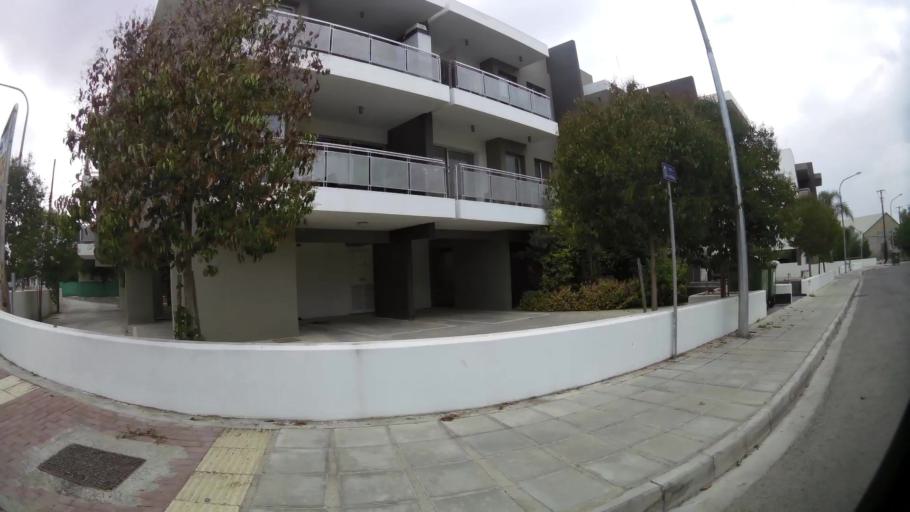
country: CY
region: Lefkosia
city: Geri
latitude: 35.1204
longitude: 33.3797
